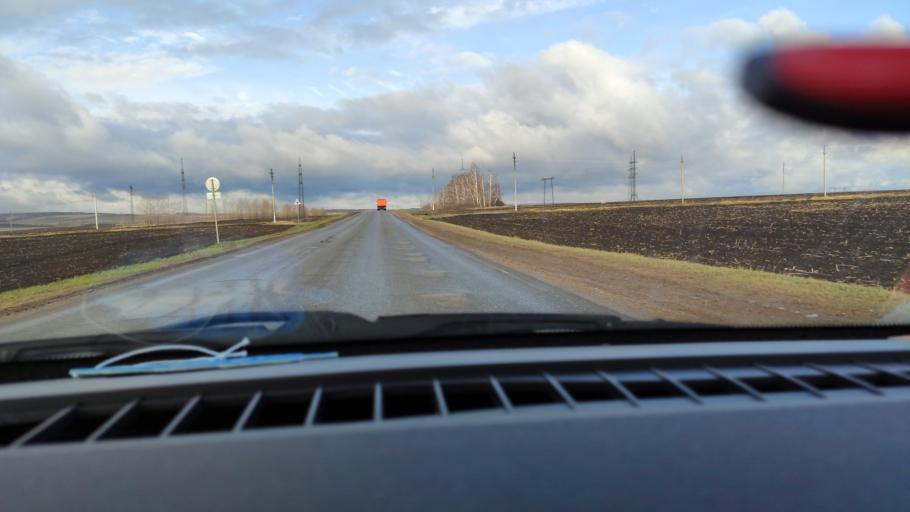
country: RU
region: Tatarstan
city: Russkiy Aktash
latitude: 55.0423
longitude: 52.0835
